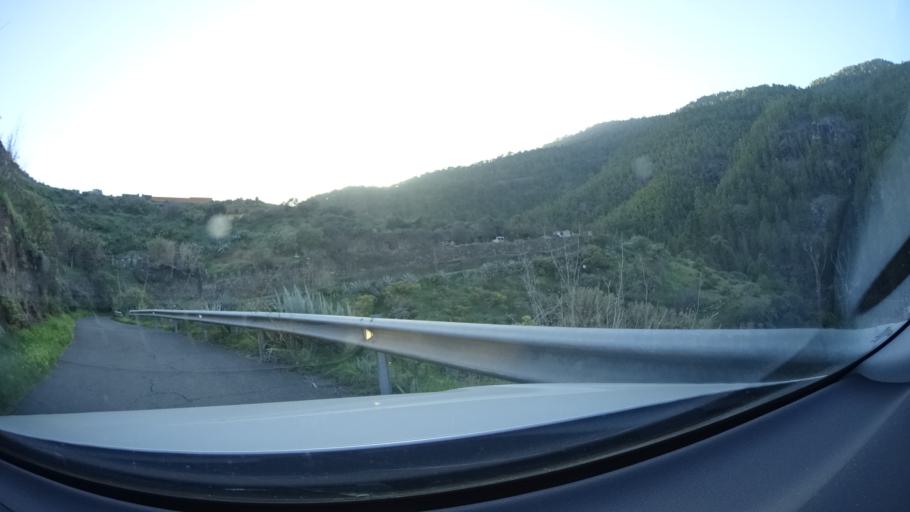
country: ES
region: Canary Islands
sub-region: Provincia de Las Palmas
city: Artenara
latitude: 28.0470
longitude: -15.6712
